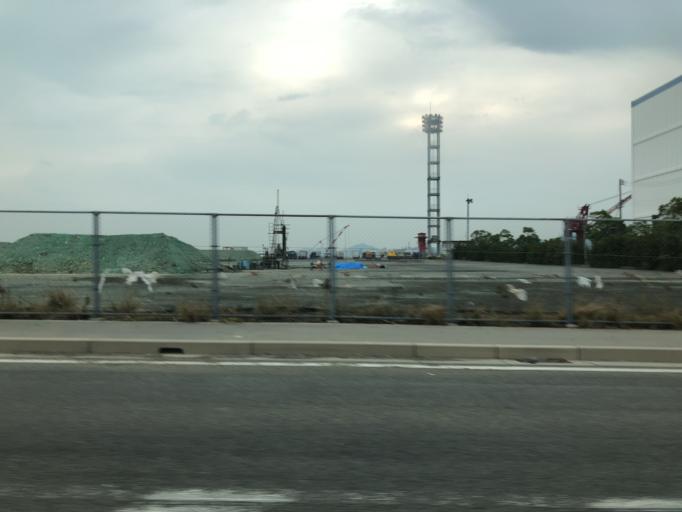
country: JP
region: Hyogo
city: Ashiya
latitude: 34.6875
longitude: 135.2555
